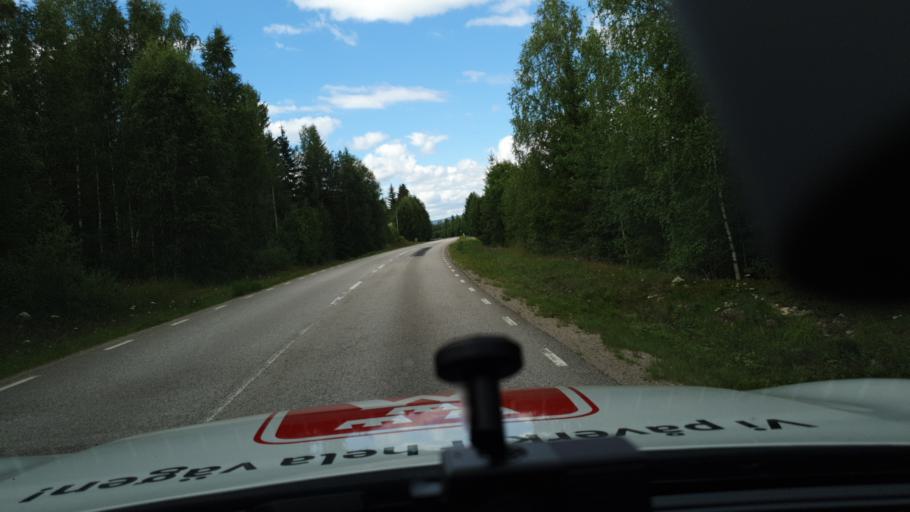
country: NO
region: Hedmark
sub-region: Trysil
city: Innbygda
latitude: 60.9131
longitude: 12.5486
